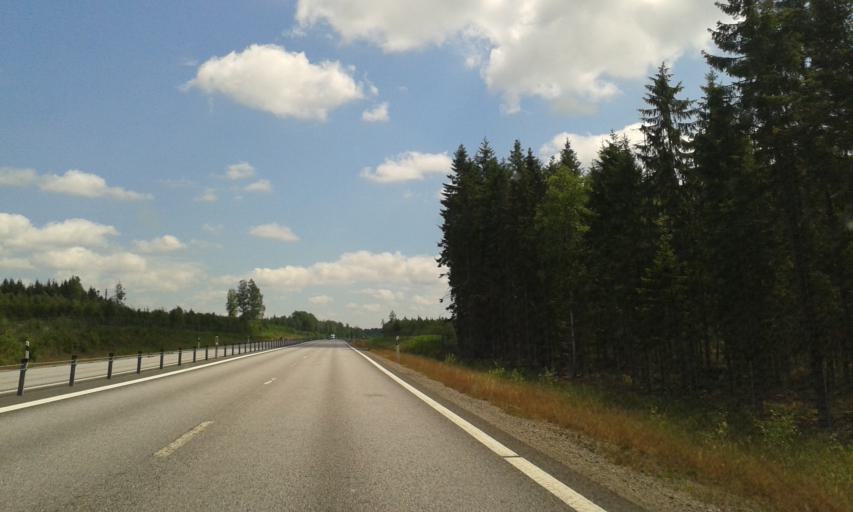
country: SE
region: Kronoberg
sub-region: Vaxjo Kommun
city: Gemla
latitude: 56.9078
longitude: 14.6492
